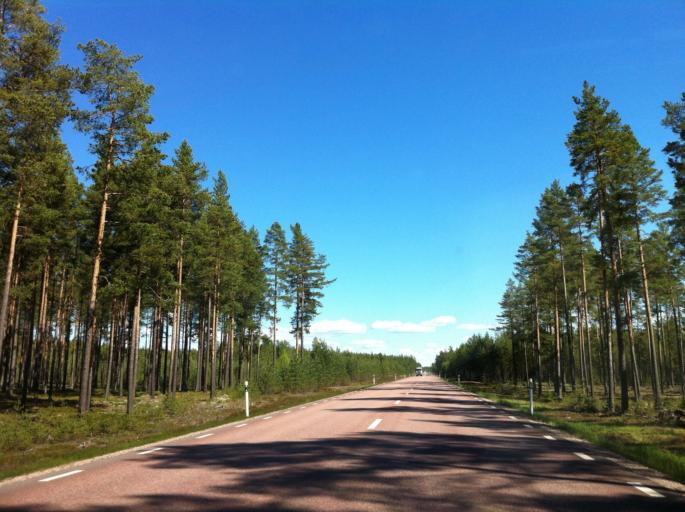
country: SE
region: Dalarna
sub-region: Mora Kommun
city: Mora
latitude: 60.9512
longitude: 14.7355
